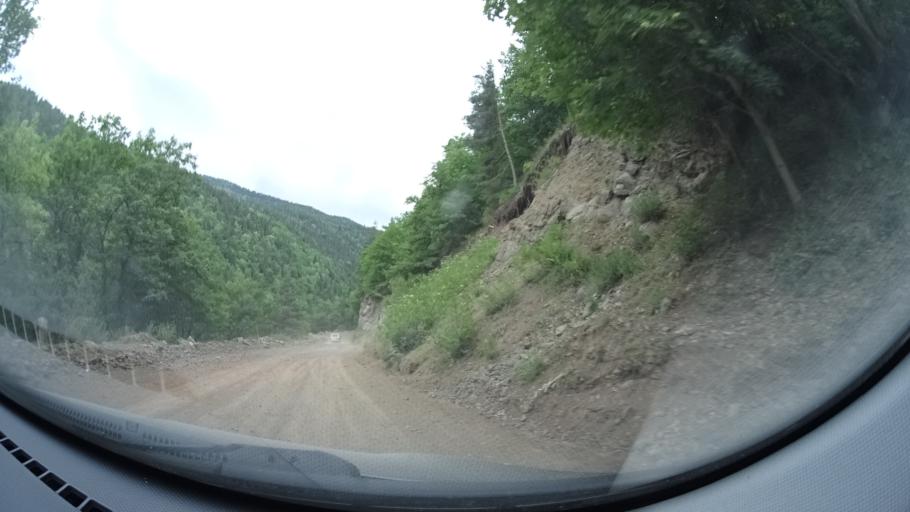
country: GE
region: Samtskhe-Javakheti
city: Adigeni
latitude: 41.6739
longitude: 42.6406
